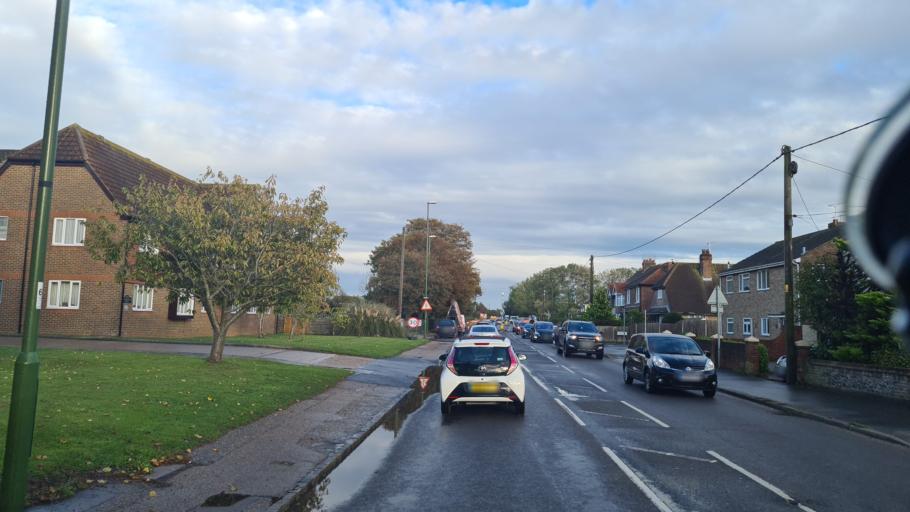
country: GB
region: England
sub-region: West Sussex
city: Littlehampton
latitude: 50.8212
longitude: -0.5419
